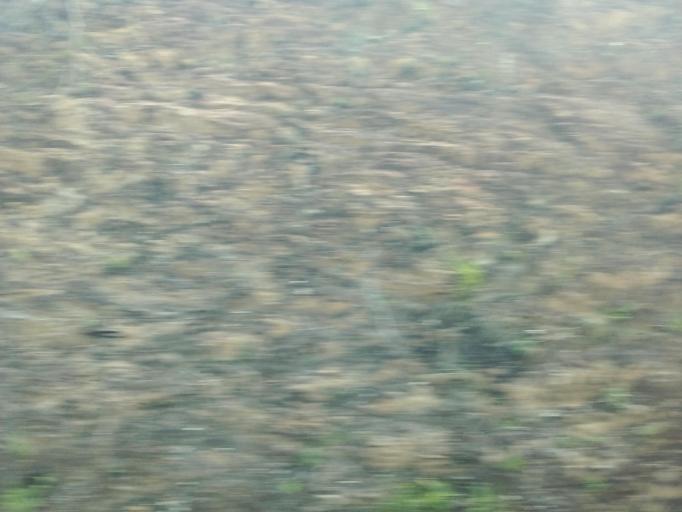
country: BR
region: Minas Gerais
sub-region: Caete
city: Caete
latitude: -19.9082
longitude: -43.6944
